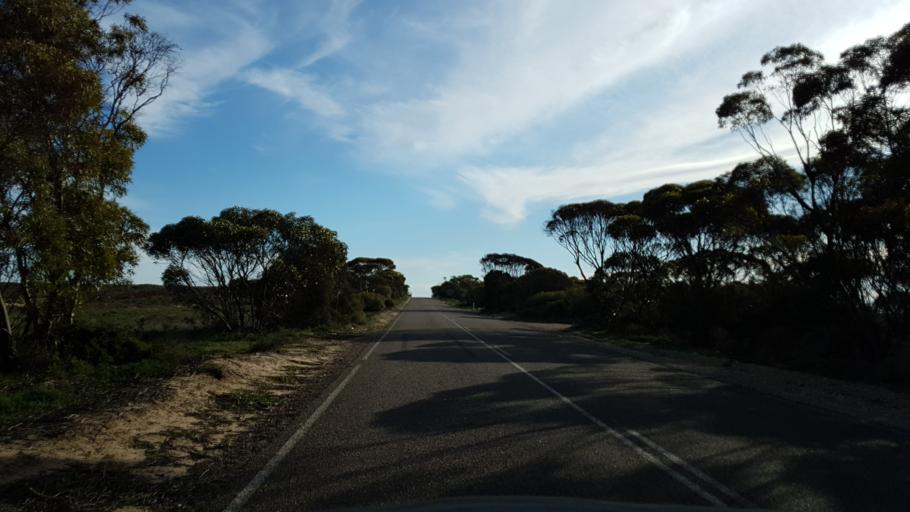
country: AU
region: South Australia
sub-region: Murray Bridge
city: Tailem Bend
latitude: -35.0641
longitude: 139.4652
